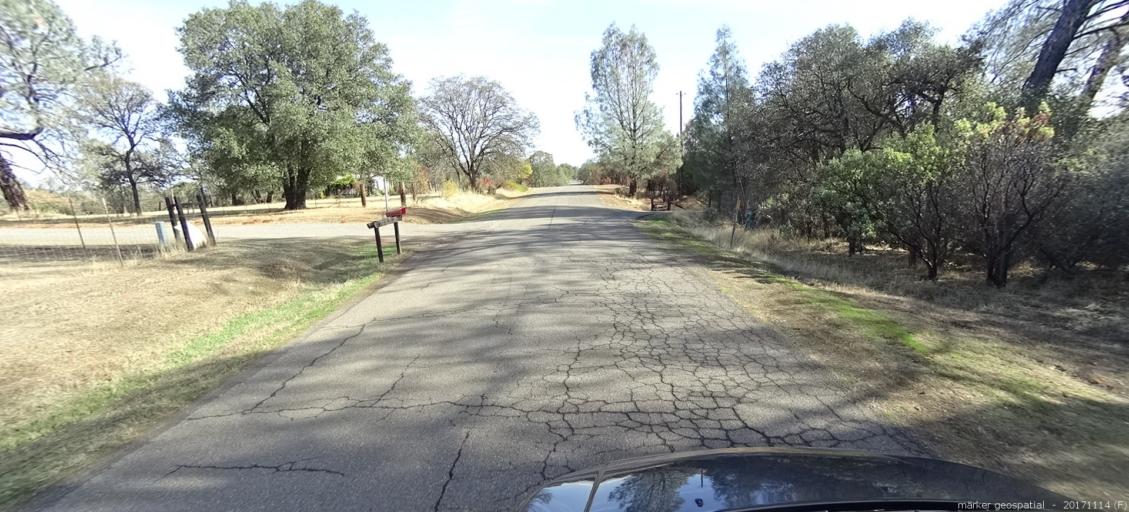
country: US
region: California
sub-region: Shasta County
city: Anderson
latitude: 40.4247
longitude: -122.3990
